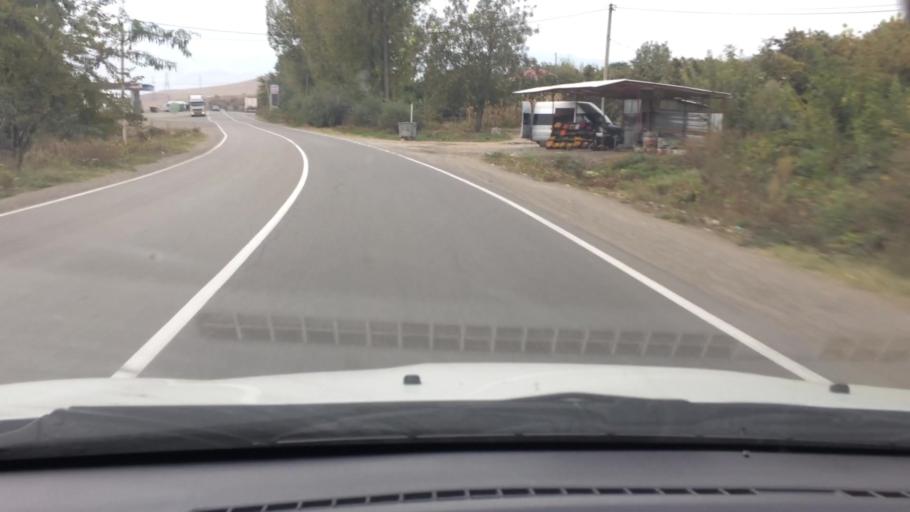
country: AM
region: Tavush
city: Bagratashen
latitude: 41.2936
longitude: 44.7878
